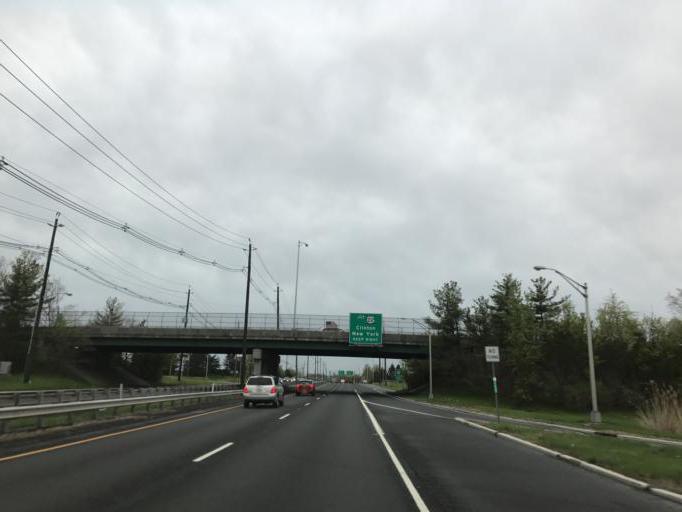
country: US
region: New Jersey
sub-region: Somerset County
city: Green Knoll
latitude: 40.5896
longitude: -74.6231
